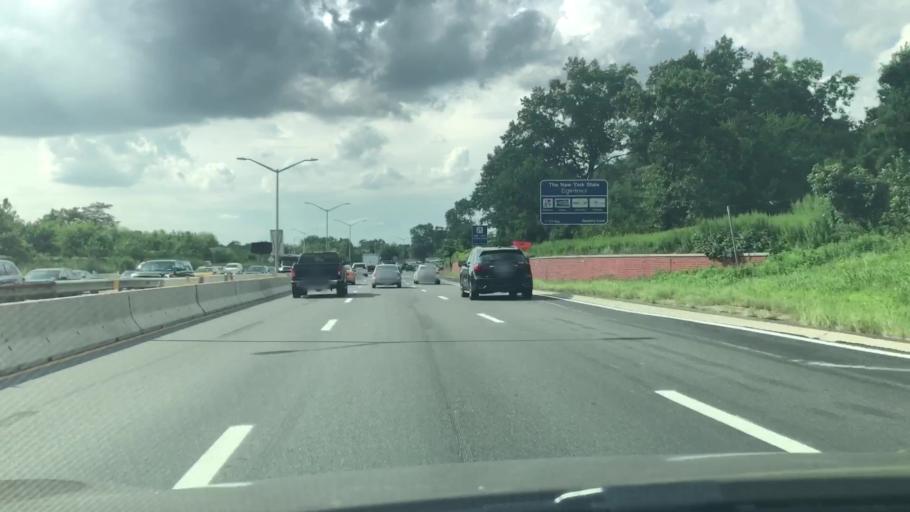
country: US
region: New York
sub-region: Queens County
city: Jamaica
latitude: 40.7250
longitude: -73.8298
